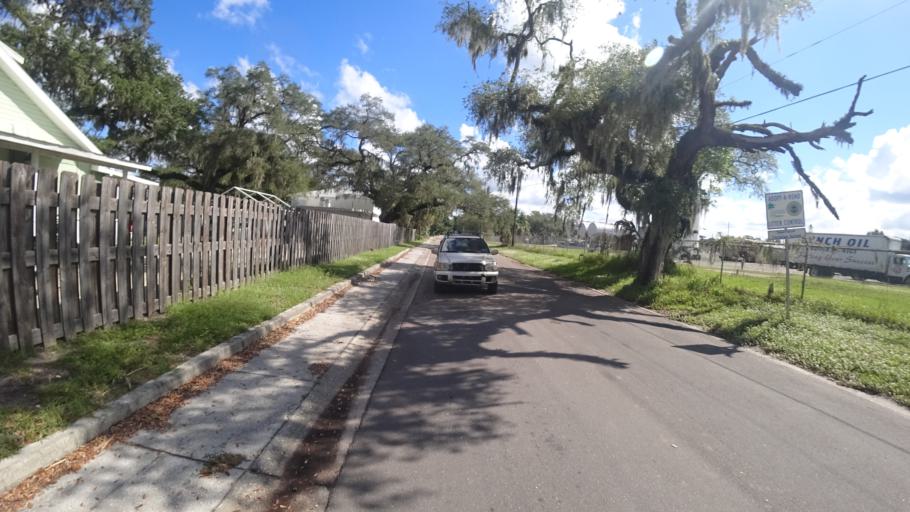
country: US
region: Florida
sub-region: Manatee County
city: West Samoset
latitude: 27.4930
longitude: -82.5503
